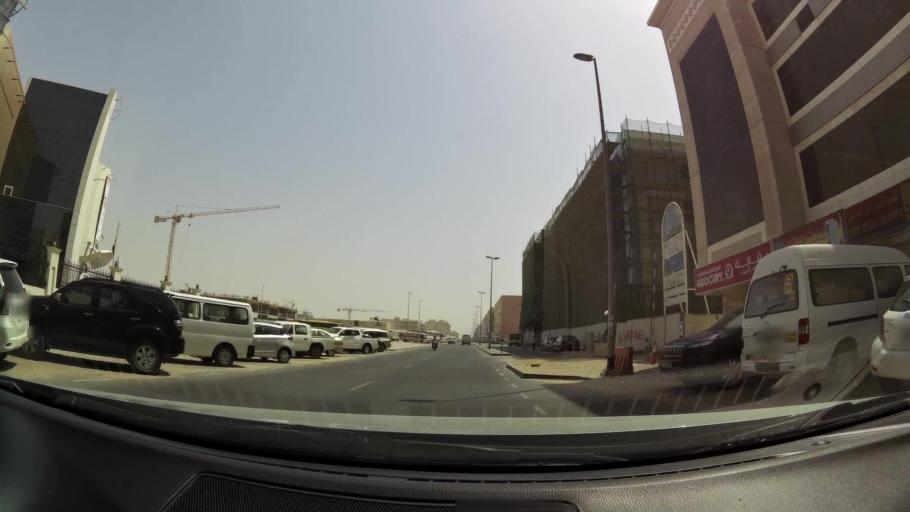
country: AE
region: Dubai
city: Dubai
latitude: 25.1559
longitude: 55.2489
